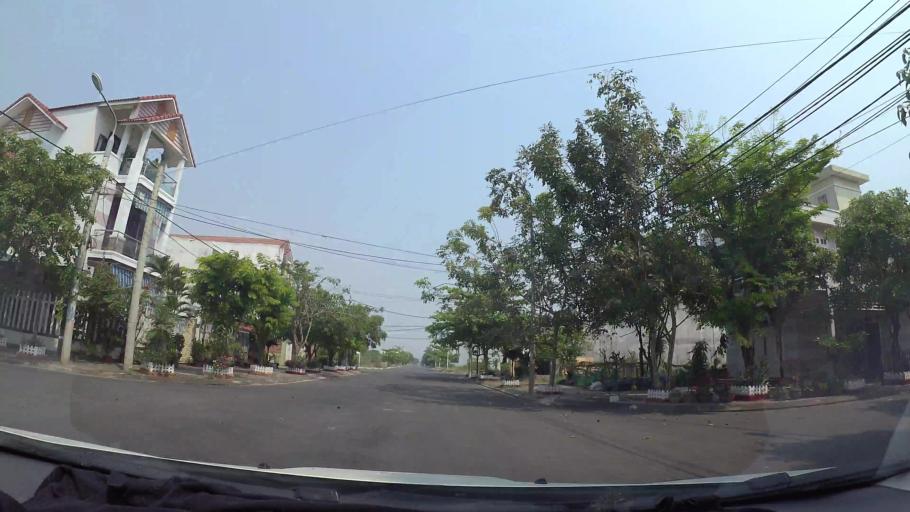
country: VN
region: Da Nang
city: Cam Le
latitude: 15.9792
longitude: 108.2142
